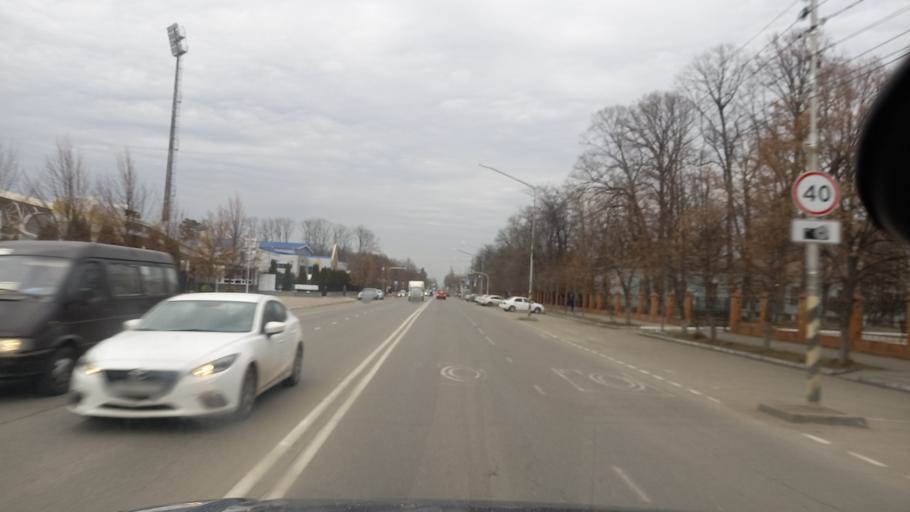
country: RU
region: Adygeya
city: Maykop
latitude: 44.5952
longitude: 40.1089
